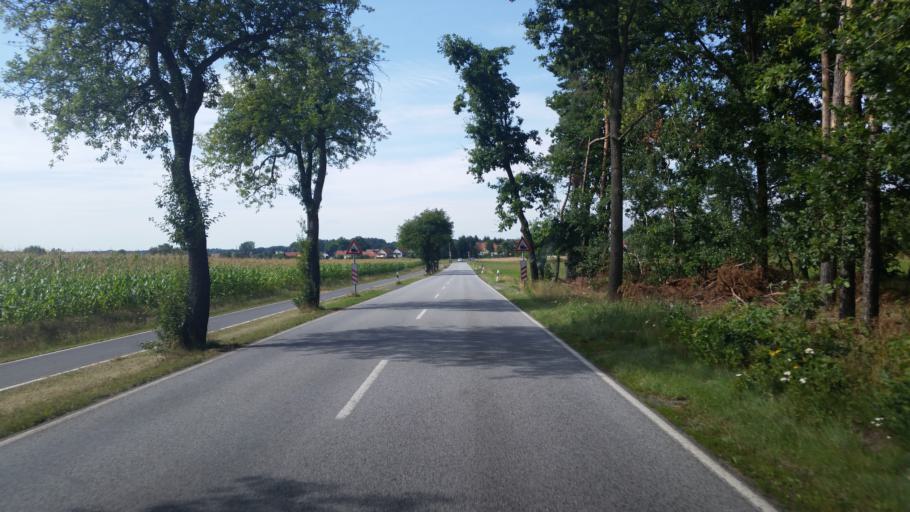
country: DE
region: Saxony
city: Bernsdorf
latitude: 51.3447
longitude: 14.0673
